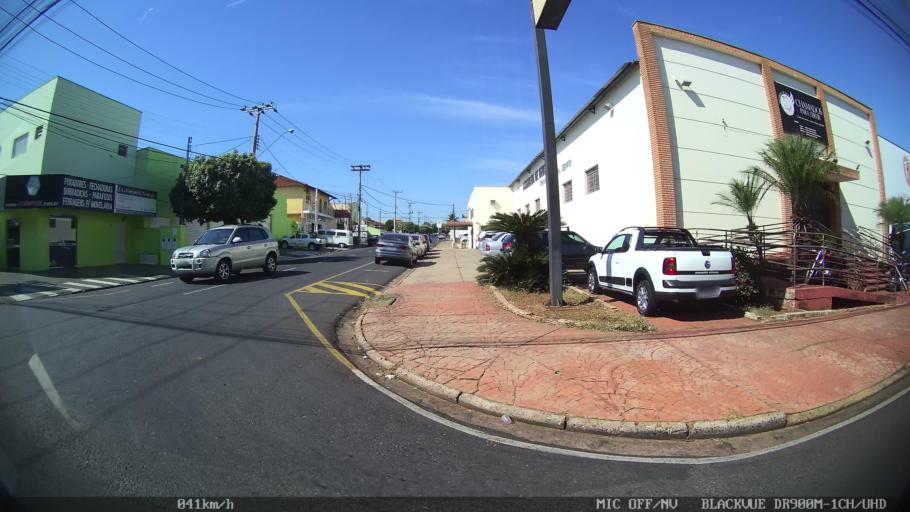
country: BR
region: Sao Paulo
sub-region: Sao Jose Do Rio Preto
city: Sao Jose do Rio Preto
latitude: -20.7974
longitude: -49.3932
